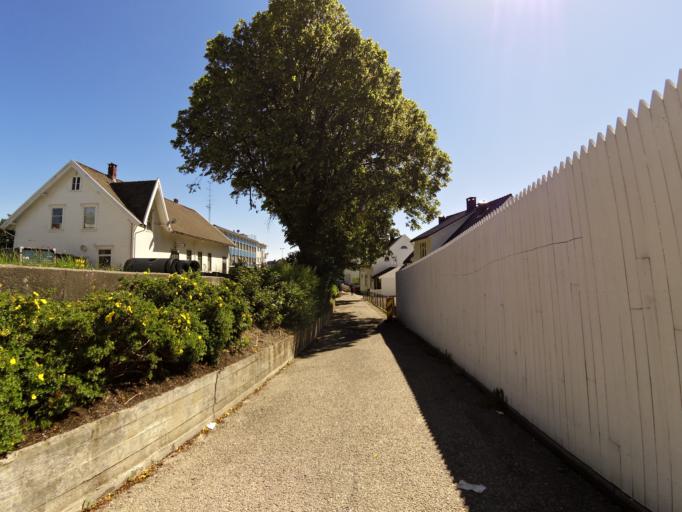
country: NO
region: Vest-Agder
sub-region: Kristiansand
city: Kristiansand
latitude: 58.1534
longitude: 8.0088
